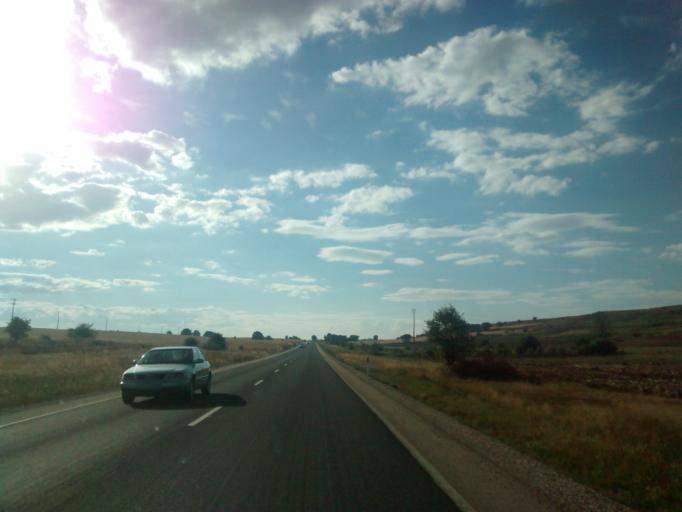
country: ES
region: Castille and Leon
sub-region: Provincia de Burgos
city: Basconcillos del Tozo
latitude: 42.6658
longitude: -3.9212
